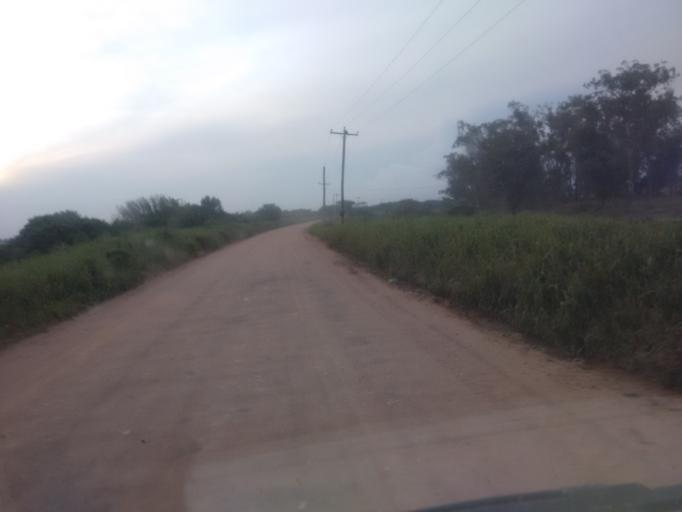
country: BR
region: Rio Grande do Sul
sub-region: Camaqua
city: Camaqua
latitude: -30.9155
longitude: -51.8055
